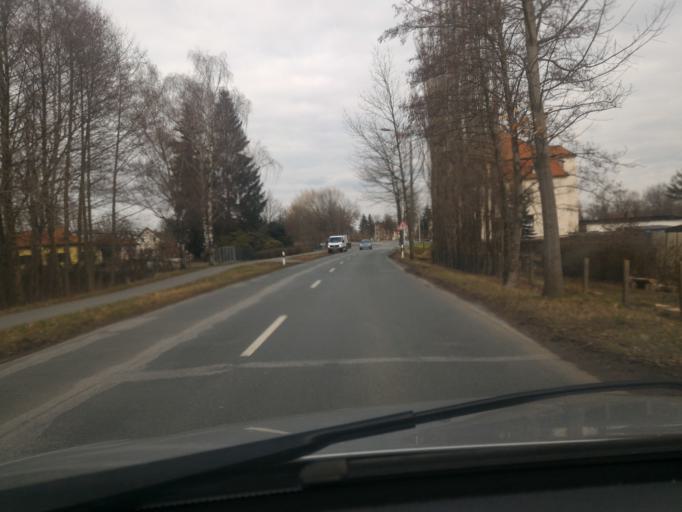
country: DE
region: Saxony
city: Zittau
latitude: 50.8757
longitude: 14.8108
